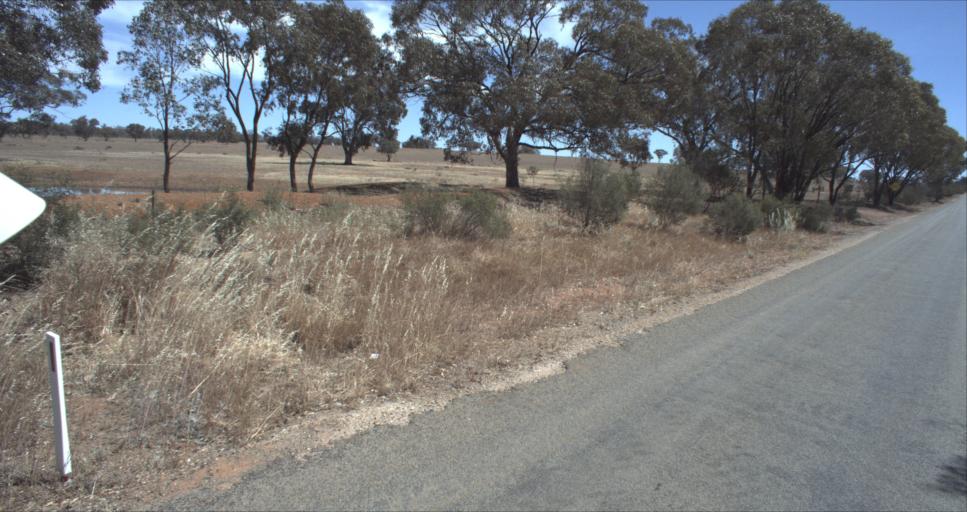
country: AU
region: New South Wales
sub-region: Leeton
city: Leeton
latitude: -34.5906
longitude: 146.4585
